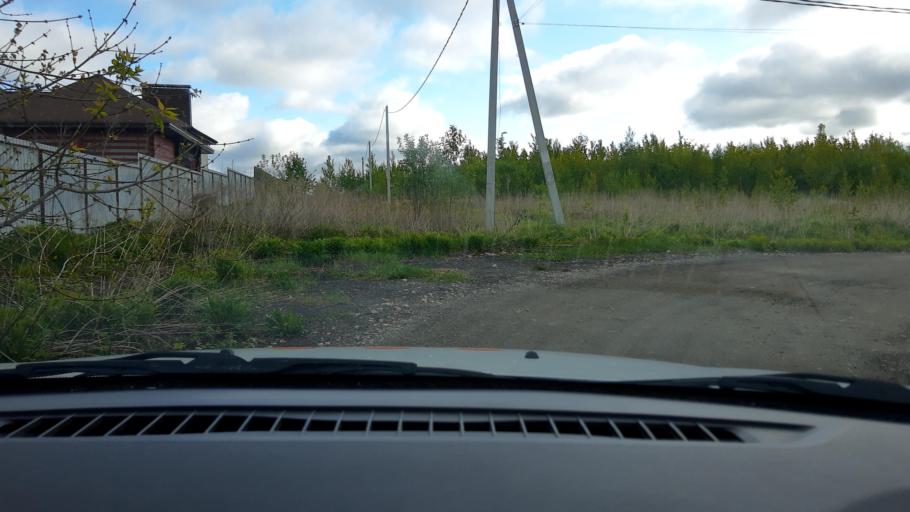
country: RU
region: Nizjnij Novgorod
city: Afonino
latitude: 56.1975
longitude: 44.0621
